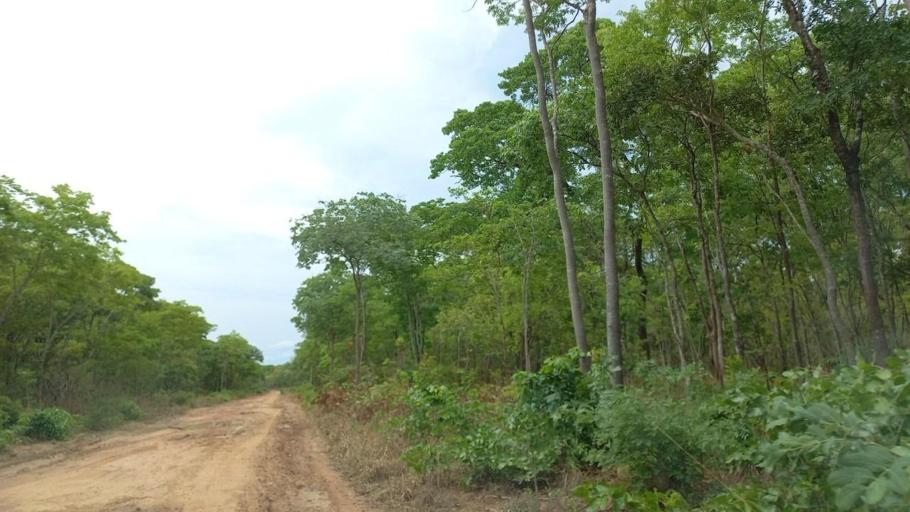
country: ZM
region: North-Western
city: Kalengwa
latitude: -13.5667
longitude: 24.9710
